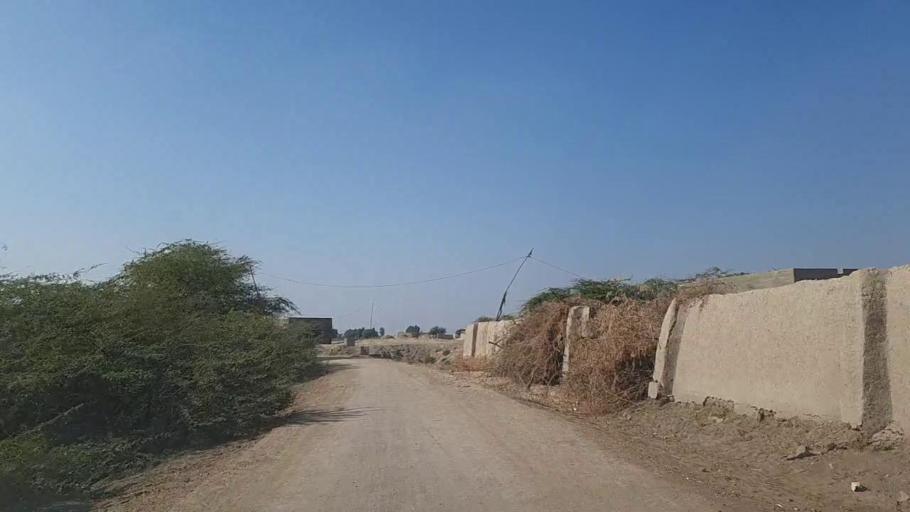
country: PK
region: Sindh
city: Digri
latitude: 25.0959
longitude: 69.2064
